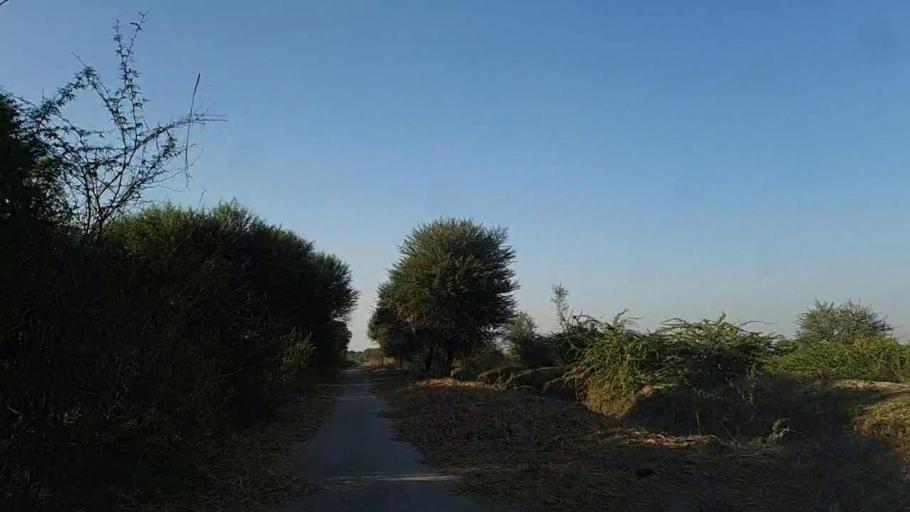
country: PK
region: Sindh
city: Samaro
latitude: 25.3452
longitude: 69.4131
